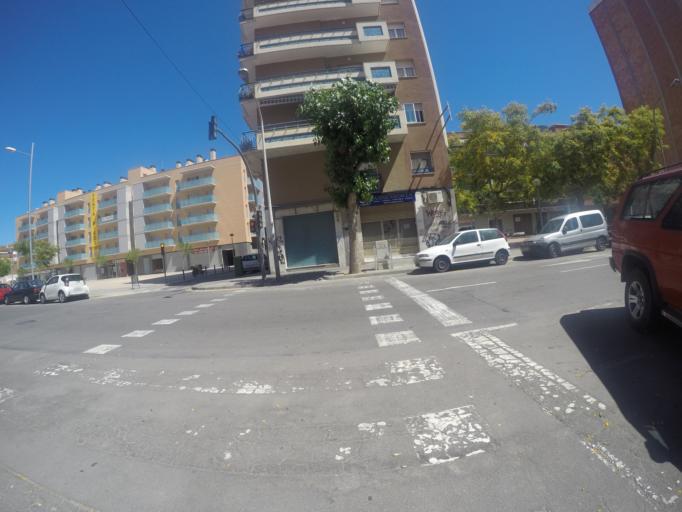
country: ES
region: Catalonia
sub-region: Provincia de Barcelona
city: Badalona
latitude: 41.4426
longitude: 2.2367
